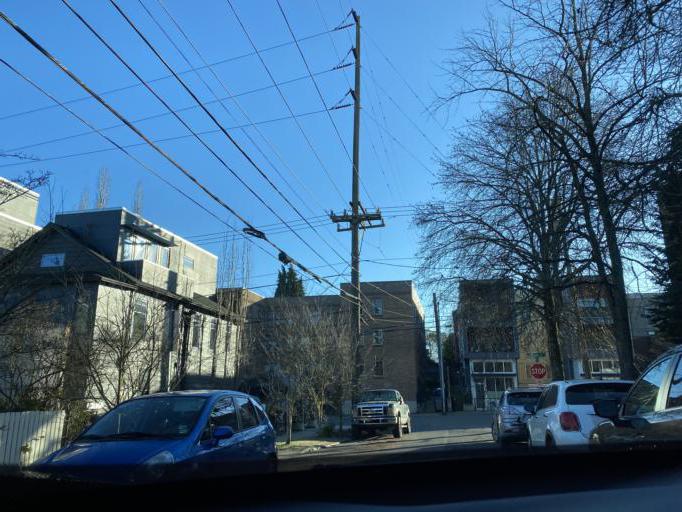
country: US
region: Washington
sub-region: King County
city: Seattle
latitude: 47.6327
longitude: -122.3611
